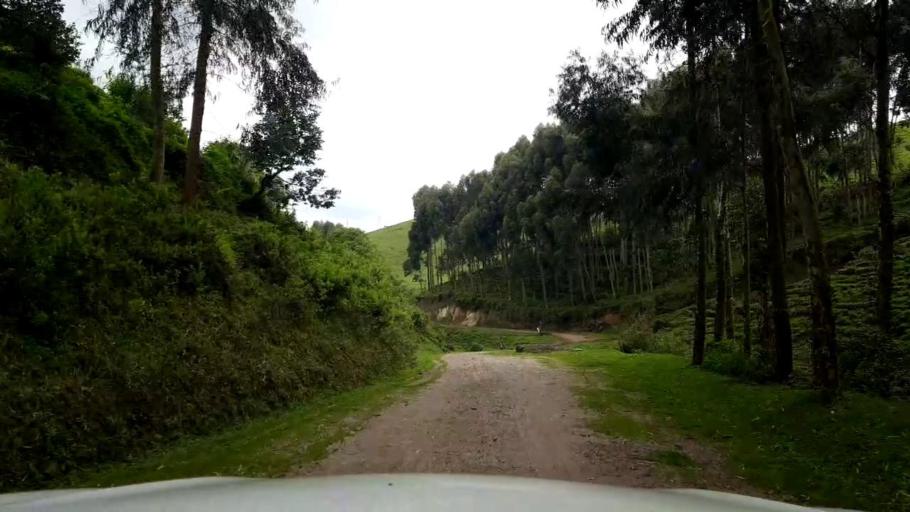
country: RW
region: Western Province
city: Gisenyi
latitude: -1.6858
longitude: 29.4179
